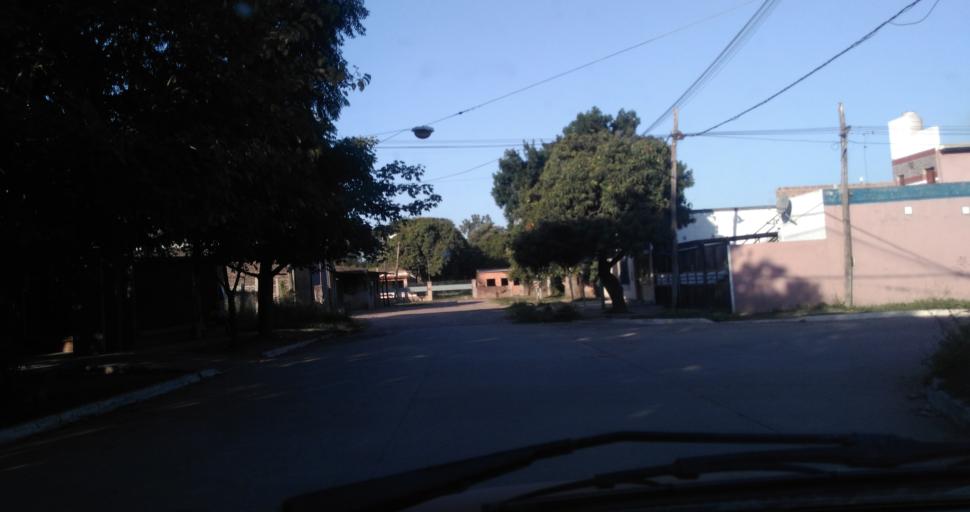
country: AR
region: Chaco
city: Fontana
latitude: -27.4147
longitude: -59.0328
